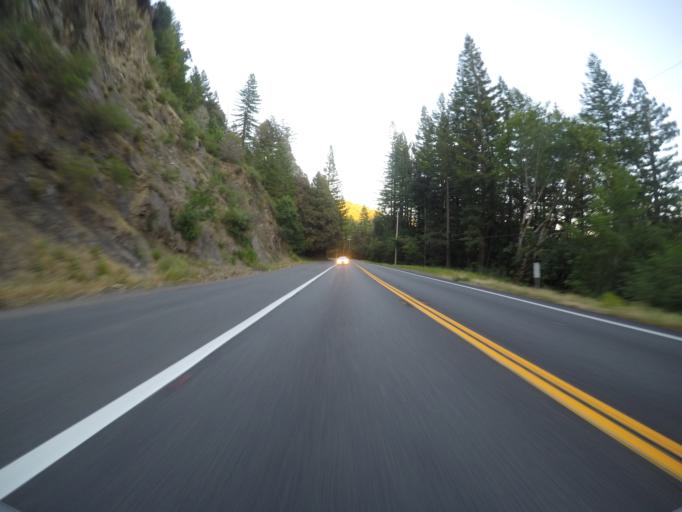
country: US
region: California
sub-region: Humboldt County
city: Redway
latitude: 39.9158
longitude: -123.7647
